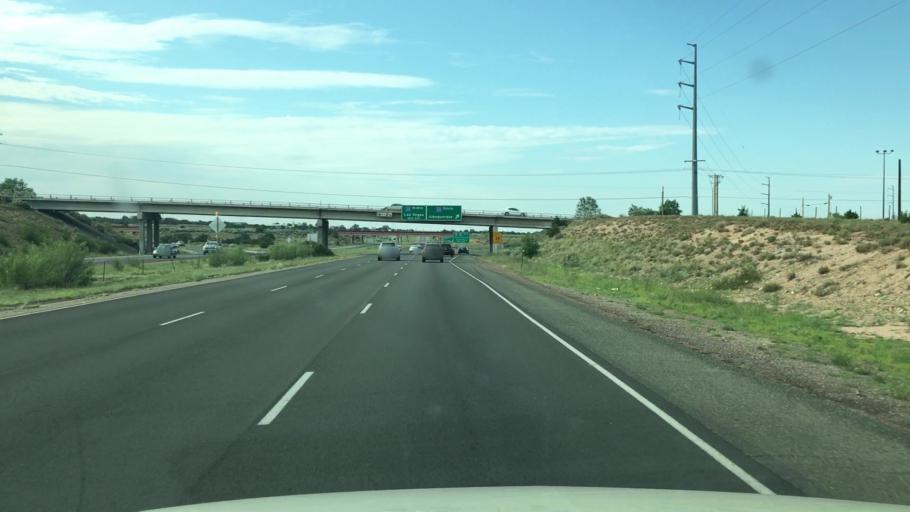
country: US
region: New Mexico
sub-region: Santa Fe County
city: Santa Fe
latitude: 35.6399
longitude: -105.9566
